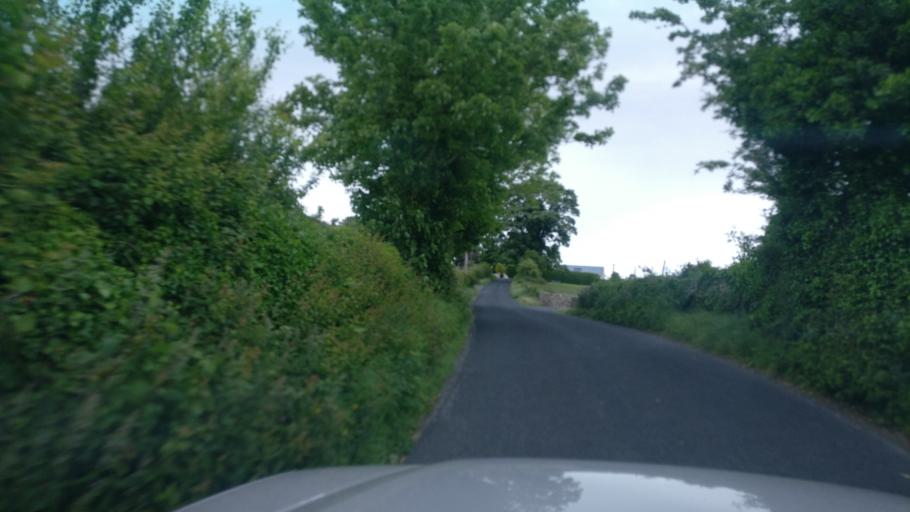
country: IE
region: Connaught
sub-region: County Galway
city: Loughrea
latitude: 53.1155
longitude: -8.4352
